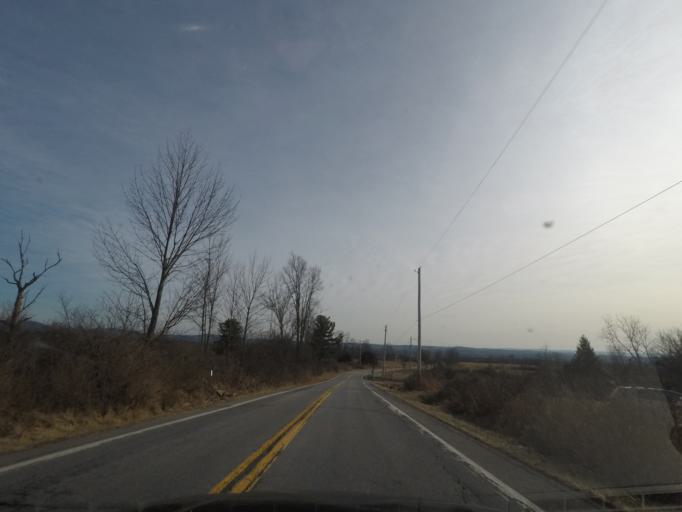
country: US
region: New York
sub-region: Saratoga County
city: Stillwater
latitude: 42.9848
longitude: -73.6503
